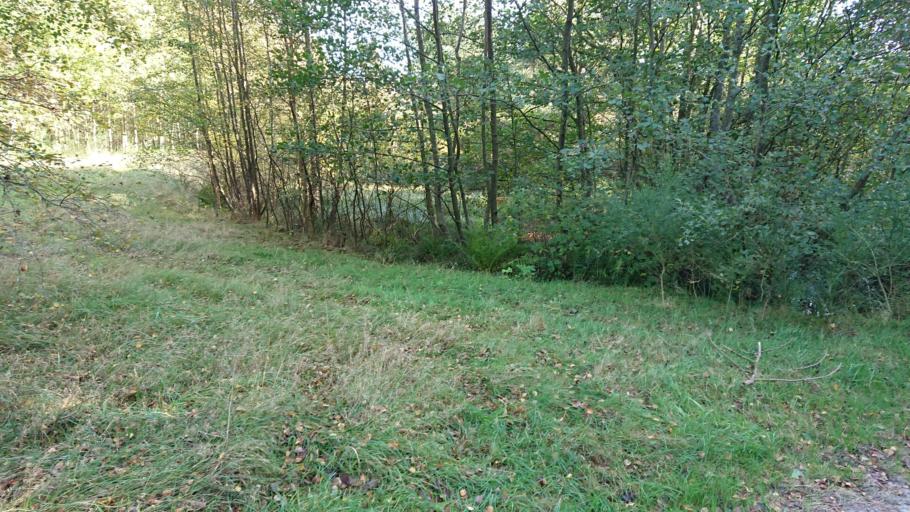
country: DK
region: North Denmark
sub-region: Frederikshavn Kommune
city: Strandby
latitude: 57.6384
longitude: 10.4490
